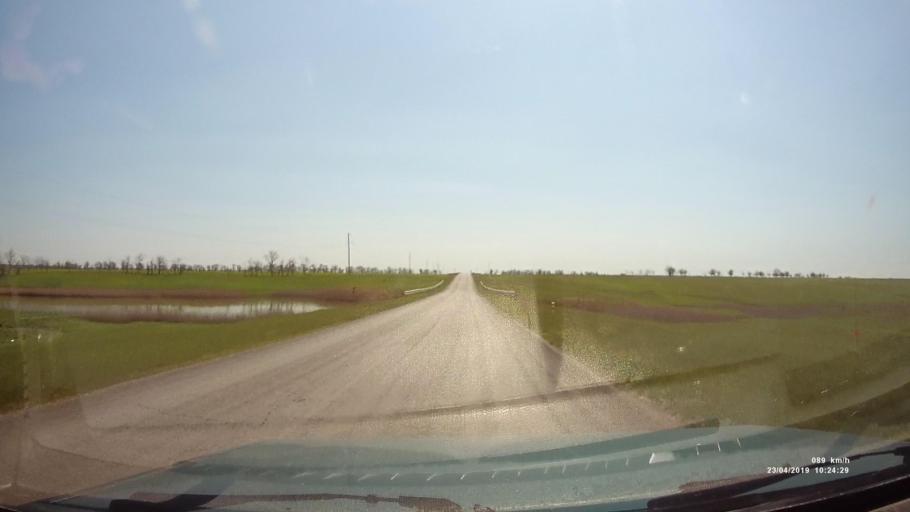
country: RU
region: Rostov
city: Sovetskoye
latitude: 46.6385
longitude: 42.4423
